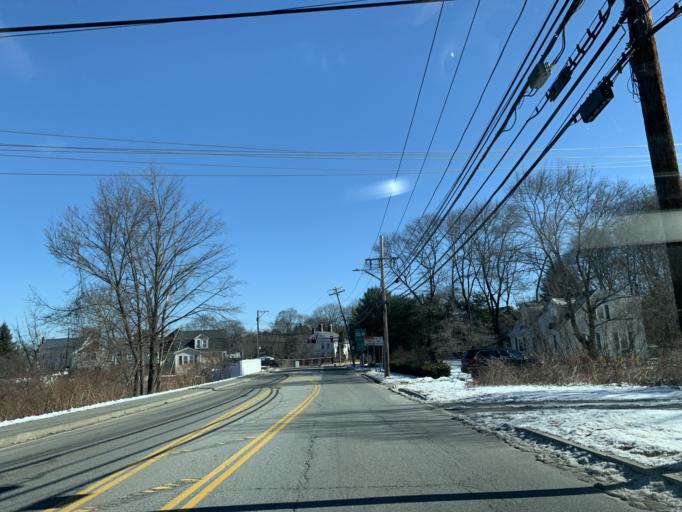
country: US
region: Massachusetts
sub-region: Middlesex County
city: Chelmsford
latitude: 42.5993
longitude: -71.3422
